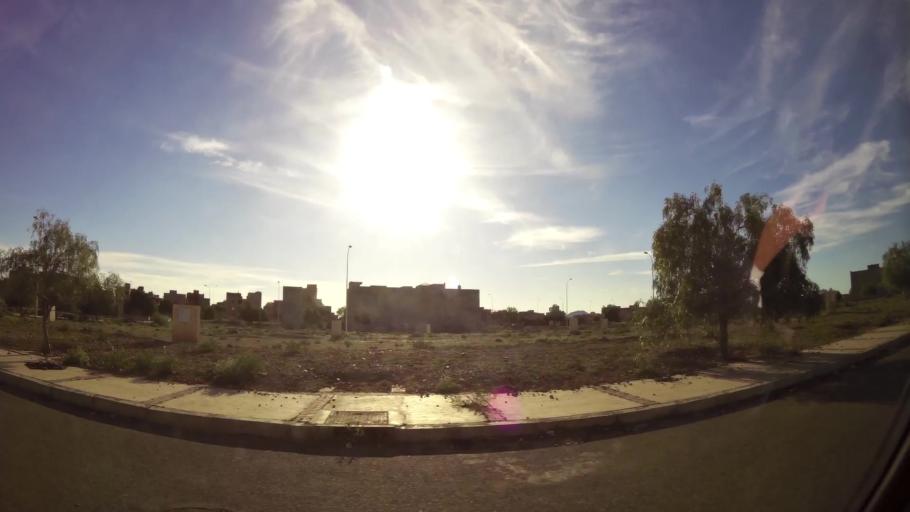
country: MA
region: Marrakech-Tensift-Al Haouz
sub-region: Marrakech
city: Marrakesh
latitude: 31.7575
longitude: -8.0946
